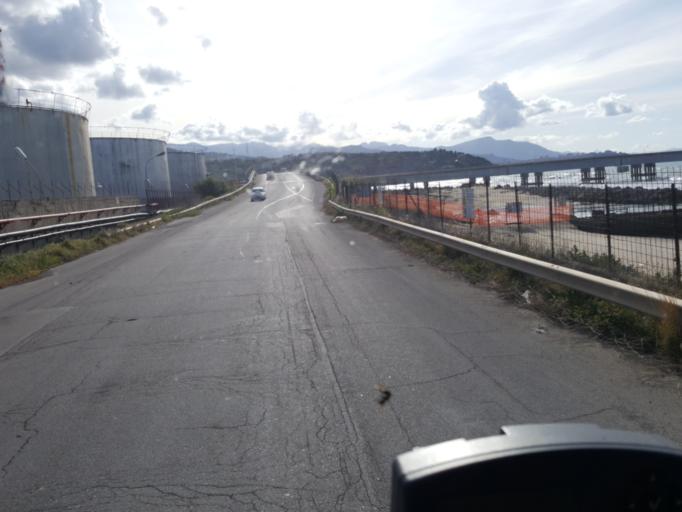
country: IT
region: Sicily
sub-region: Palermo
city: Sciara
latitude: 37.9707
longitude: 13.7555
